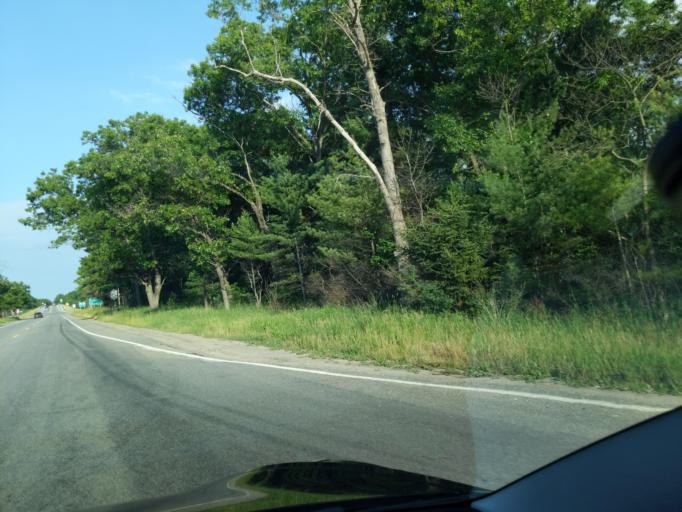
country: US
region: Michigan
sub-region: Muskegon County
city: Lakewood Club
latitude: 43.3839
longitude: -86.2864
